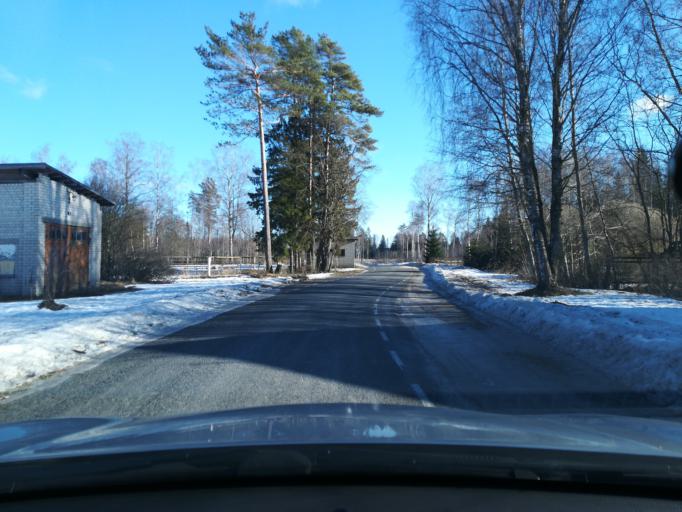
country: EE
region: Raplamaa
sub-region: Kohila vald
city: Kohila
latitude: 59.2268
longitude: 24.7159
